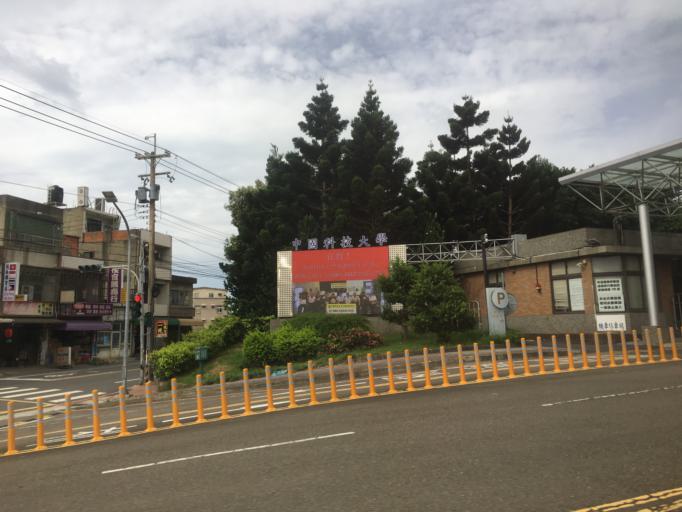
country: TW
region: Taiwan
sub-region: Hsinchu
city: Zhubei
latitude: 24.9193
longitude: 121.0548
